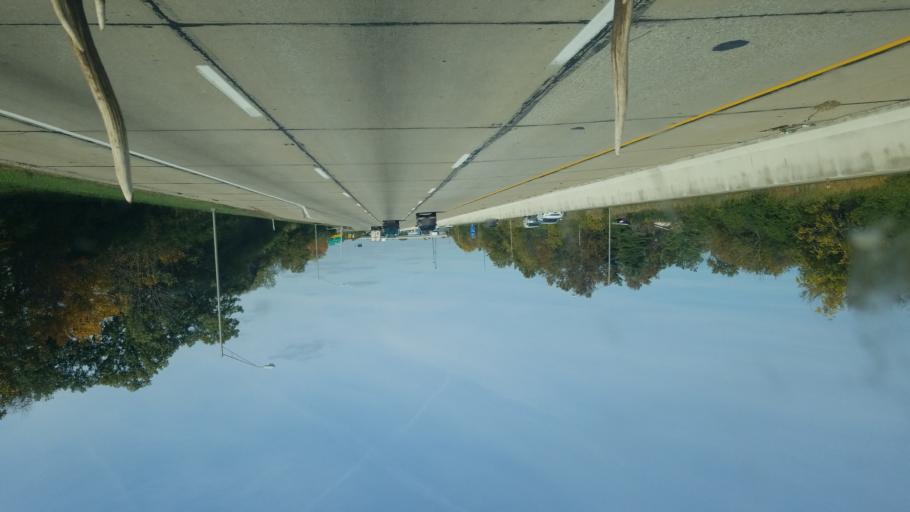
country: US
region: Indiana
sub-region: Marion County
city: Speedway
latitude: 39.7267
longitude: -86.2485
